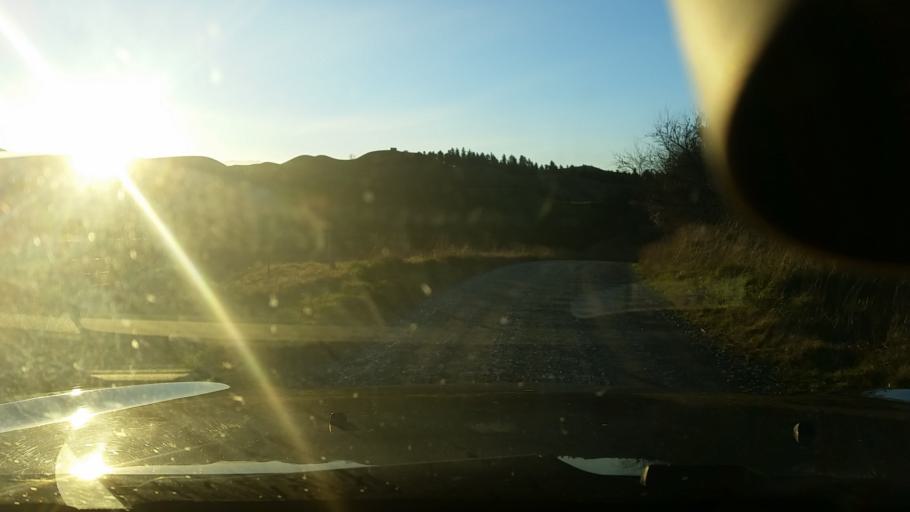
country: NZ
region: Marlborough
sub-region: Marlborough District
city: Blenheim
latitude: -41.7322
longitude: 174.0371
